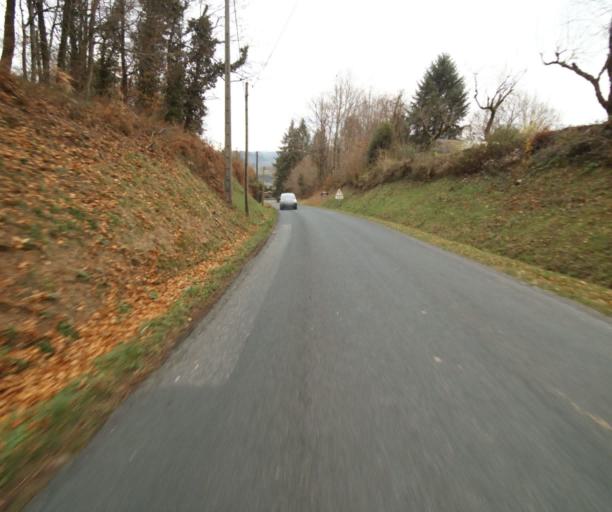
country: FR
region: Limousin
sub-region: Departement de la Correze
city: Tulle
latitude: 45.2618
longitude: 1.7354
